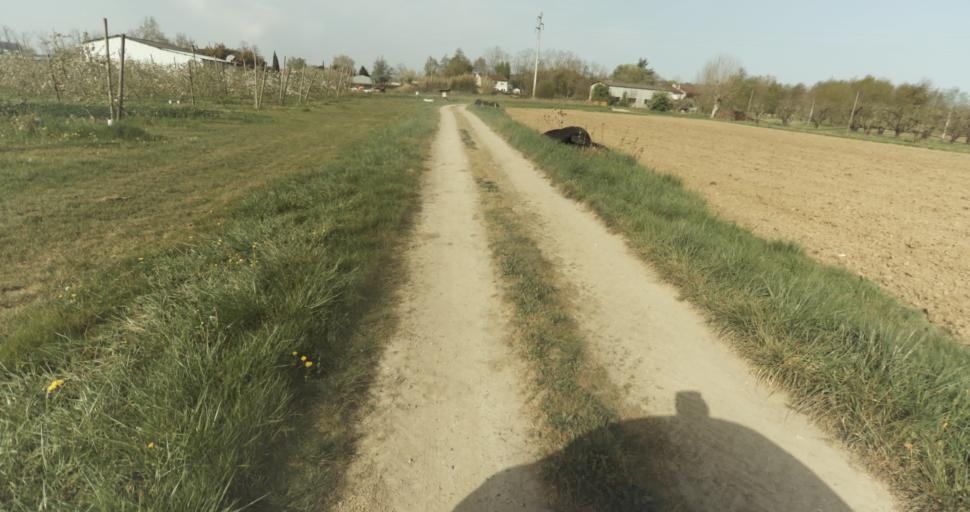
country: FR
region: Midi-Pyrenees
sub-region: Departement du Tarn-et-Garonne
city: Moissac
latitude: 44.1084
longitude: 1.1190
